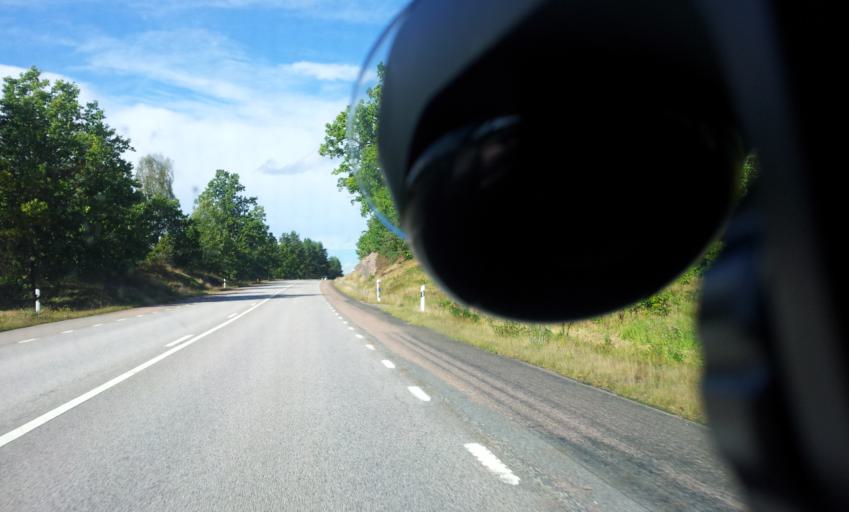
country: SE
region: Kalmar
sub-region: Vasterviks Kommun
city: Ankarsrum
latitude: 57.6063
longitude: 16.4762
